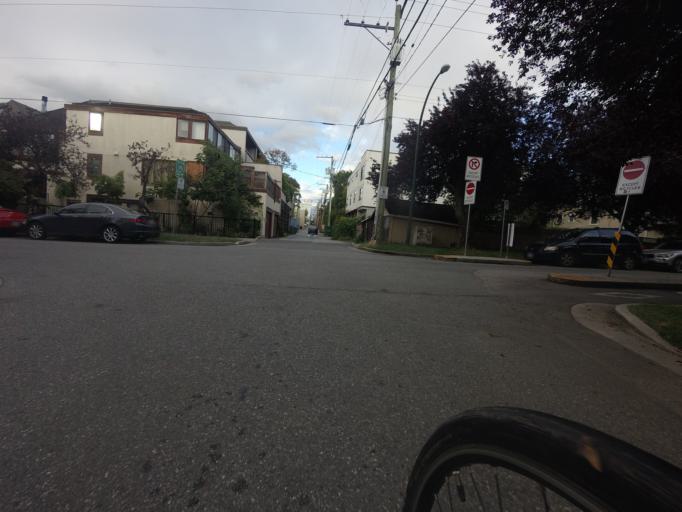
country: CA
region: British Columbia
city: West End
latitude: 49.2703
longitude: -123.1480
